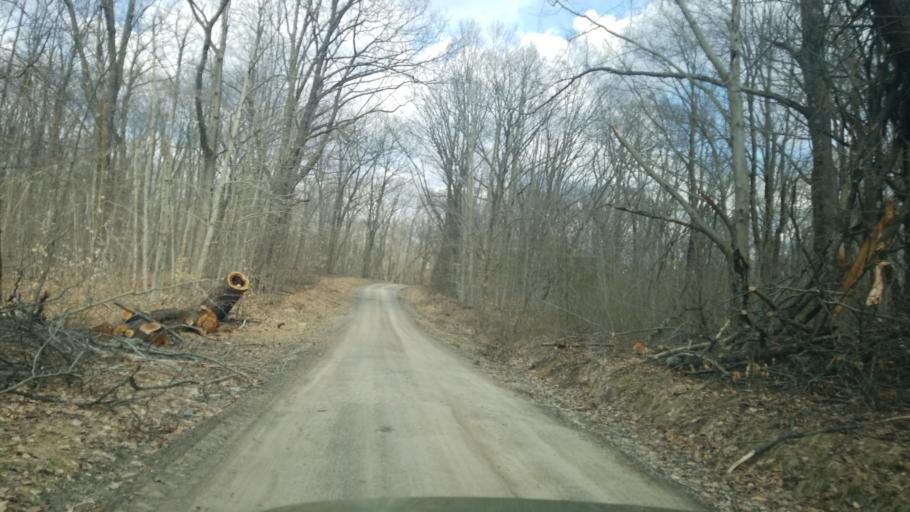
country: US
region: Pennsylvania
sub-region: Clearfield County
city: Clearfield
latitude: 41.1551
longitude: -78.5167
